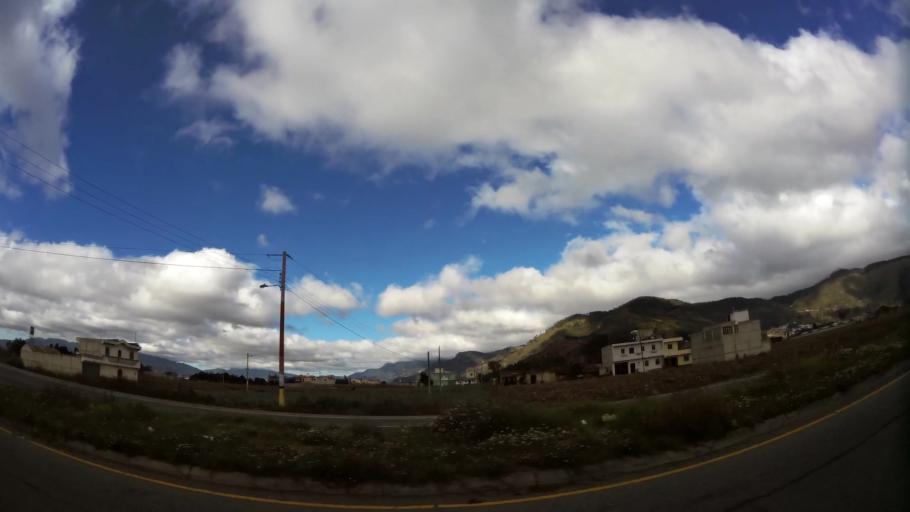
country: GT
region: Quetzaltenango
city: Salcaja
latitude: 14.8833
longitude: -91.4701
